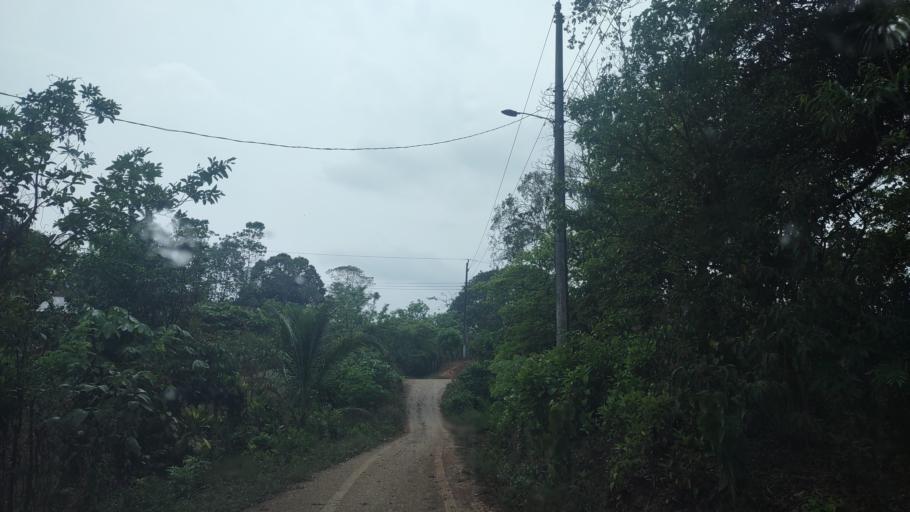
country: MX
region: Veracruz
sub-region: Uxpanapa
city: Poblado 10
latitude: 17.4475
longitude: -94.0979
